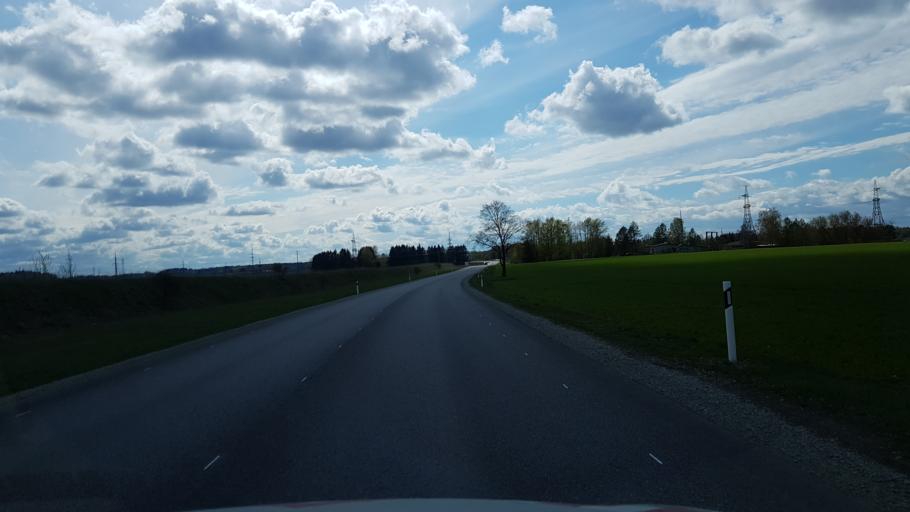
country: EE
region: Laeaene-Virumaa
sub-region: Rakvere linn
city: Rakvere
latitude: 59.3207
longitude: 26.3414
